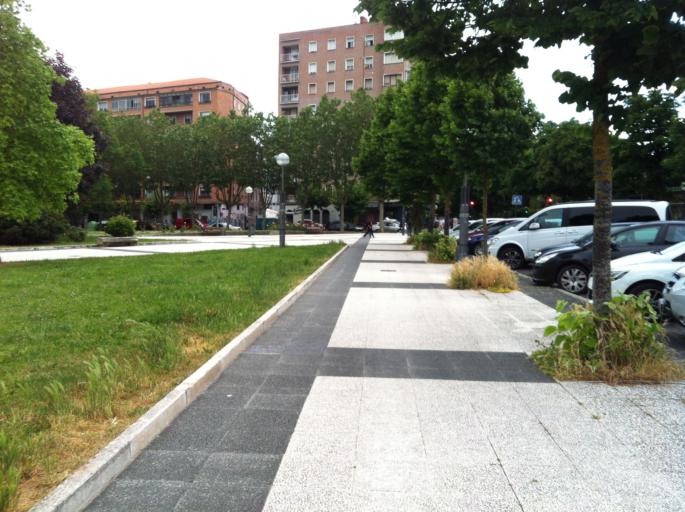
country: ES
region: Basque Country
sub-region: Provincia de Alava
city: Gasteiz / Vitoria
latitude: 42.8379
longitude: -2.6670
